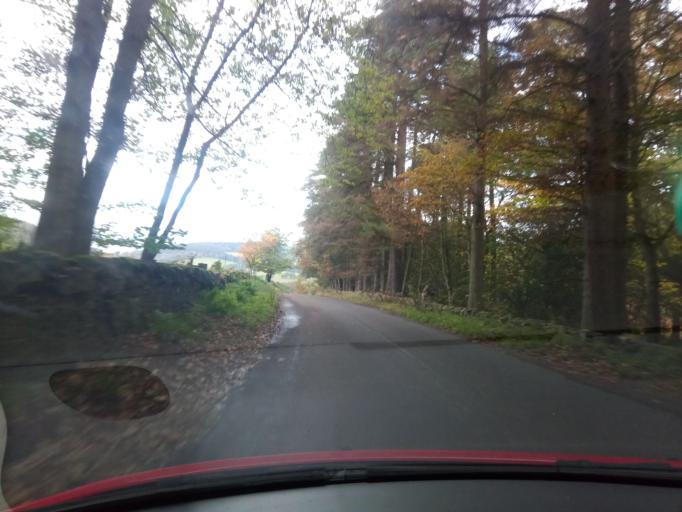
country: GB
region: Scotland
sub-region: The Scottish Borders
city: Peebles
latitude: 55.6347
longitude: -3.1471
